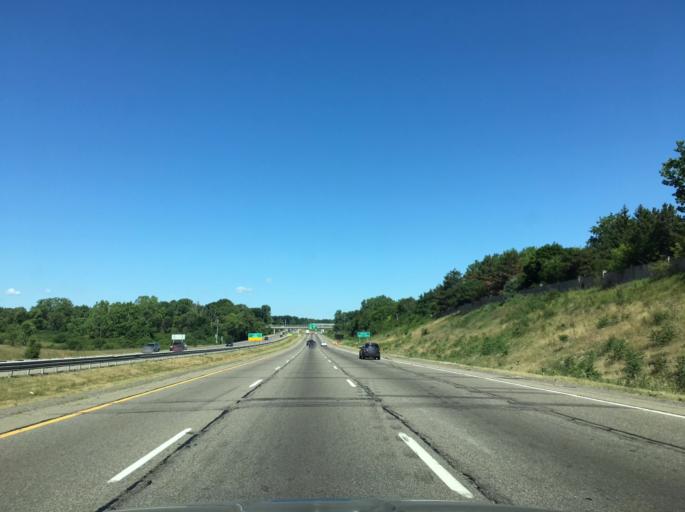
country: US
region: Michigan
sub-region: Oakland County
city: Bloomfield Hills
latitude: 42.6087
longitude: -83.2160
